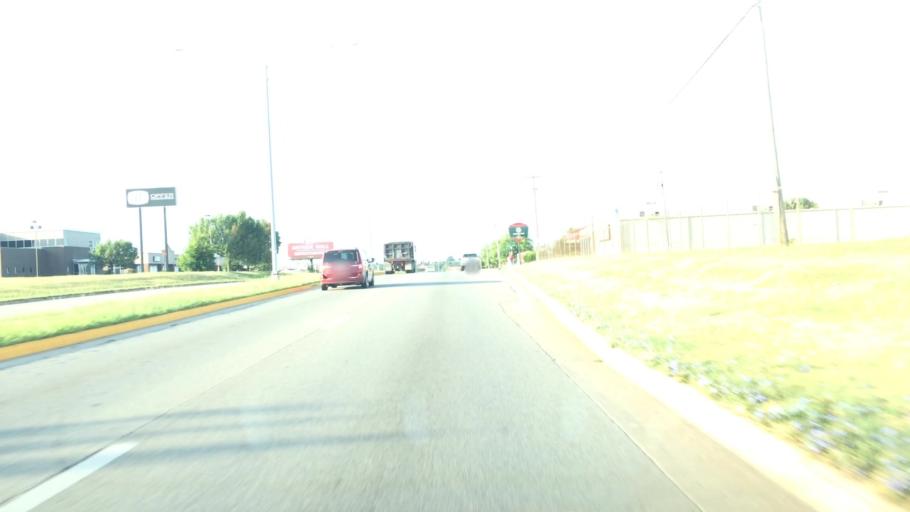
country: US
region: Missouri
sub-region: Greene County
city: Springfield
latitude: 37.1636
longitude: -93.3164
